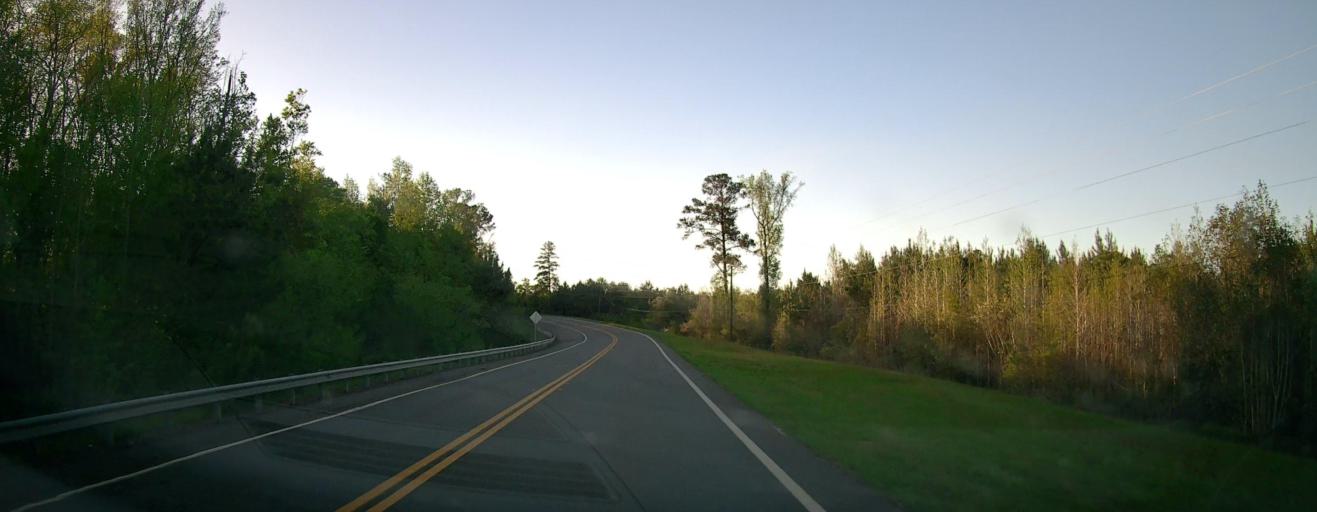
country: US
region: Georgia
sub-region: Macon County
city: Oglethorpe
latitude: 32.3102
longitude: -84.1623
